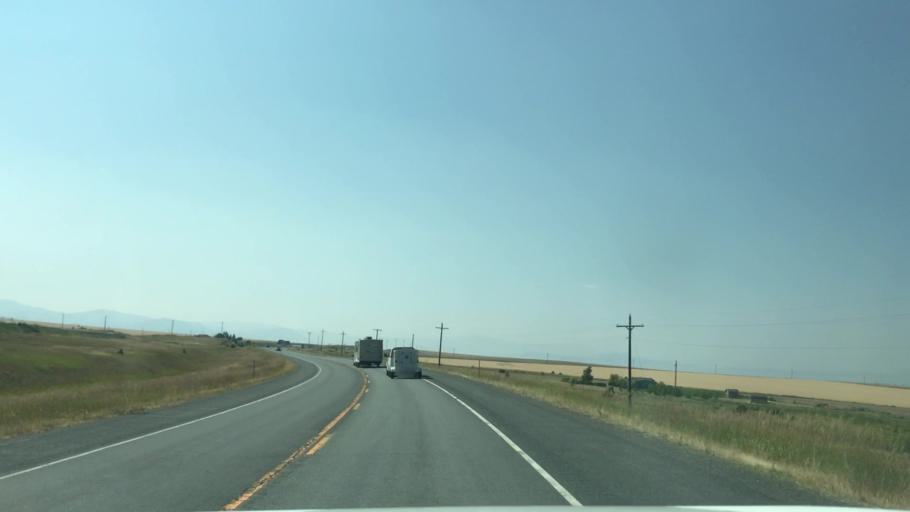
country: US
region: Montana
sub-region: Lewis and Clark County
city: East Helena
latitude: 46.5615
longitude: -111.7827
